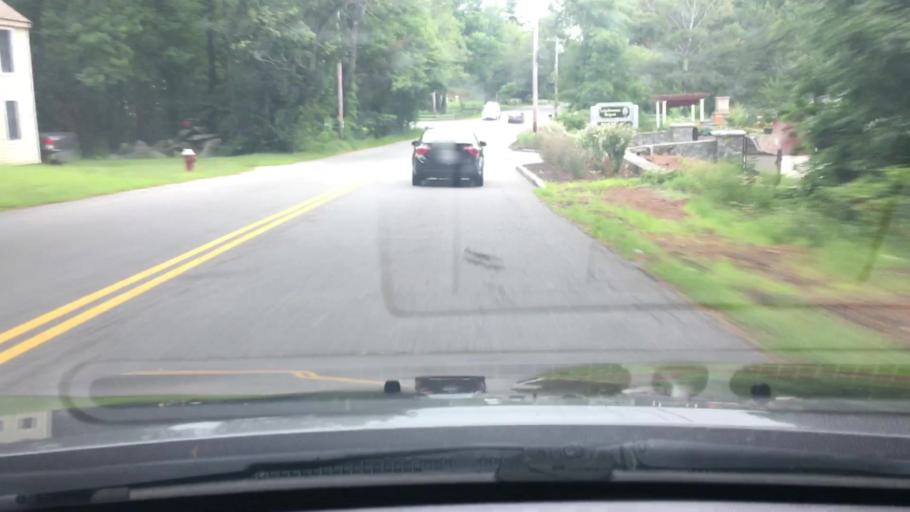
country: US
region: Massachusetts
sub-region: Worcester County
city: Milford
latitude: 42.1606
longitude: -71.5156
